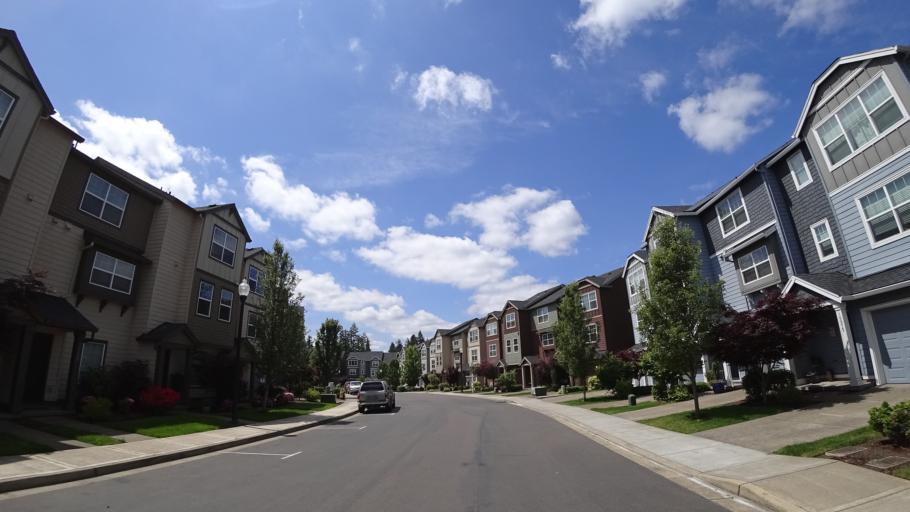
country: US
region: Oregon
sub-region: Washington County
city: King City
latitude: 45.4407
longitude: -122.8164
